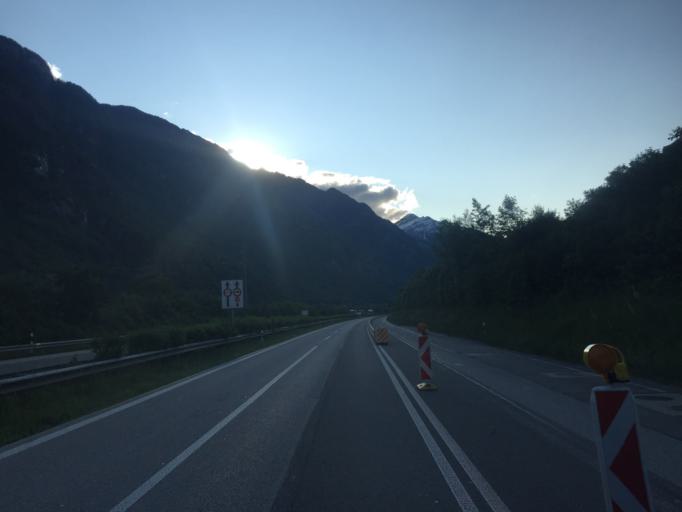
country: CH
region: Ticino
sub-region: Riviera District
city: Biasca
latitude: 46.3618
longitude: 8.9432
